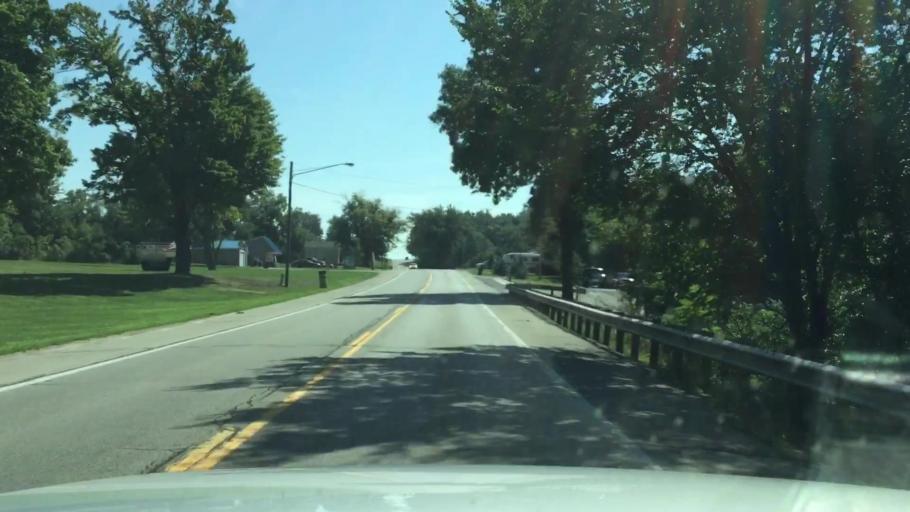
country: US
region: Michigan
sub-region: Lenawee County
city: Manitou Beach-Devils Lake
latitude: 42.0063
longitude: -84.2876
